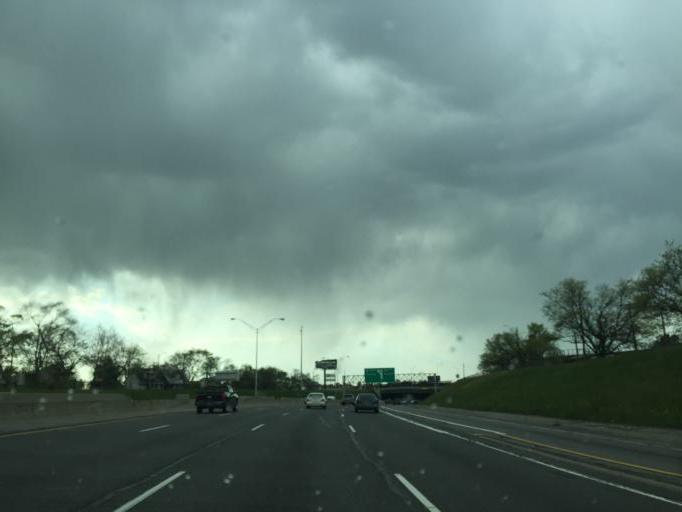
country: US
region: Michigan
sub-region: Wayne County
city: Dearborn
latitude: 42.3689
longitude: -83.1425
